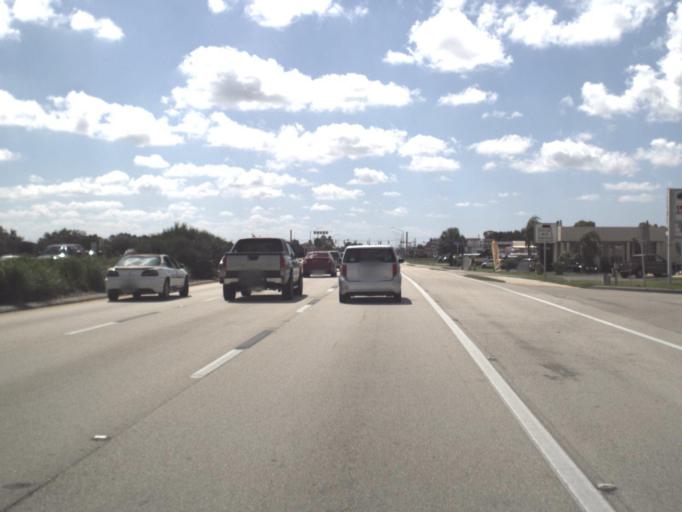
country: US
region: Florida
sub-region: Lee County
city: Pine Manor
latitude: 26.5806
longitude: -81.8720
